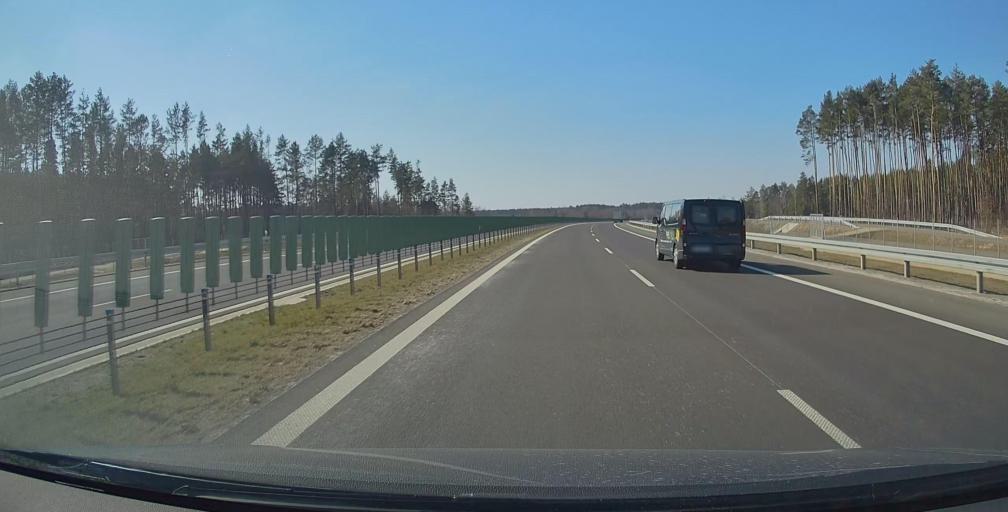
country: PL
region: Subcarpathian Voivodeship
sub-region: Powiat nizanski
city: Raclawice
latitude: 50.4779
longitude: 22.1822
